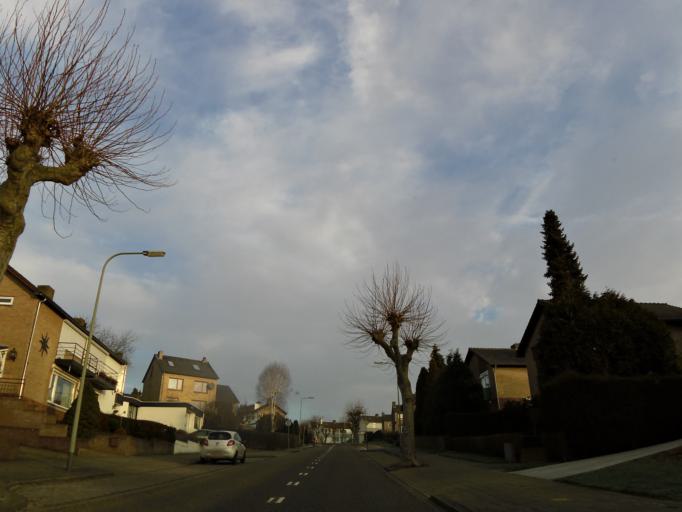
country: NL
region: Limburg
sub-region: Gemeente Simpelveld
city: Simpelveld
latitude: 50.8362
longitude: 5.9768
